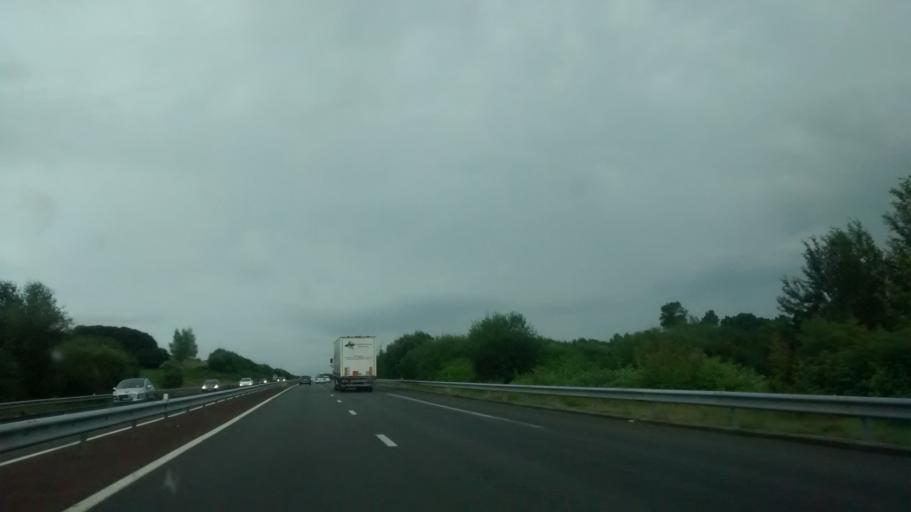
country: FR
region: Lower Normandy
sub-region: Departement de la Manche
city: Villedieu-les-Poeles
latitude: 48.7942
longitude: -1.2644
